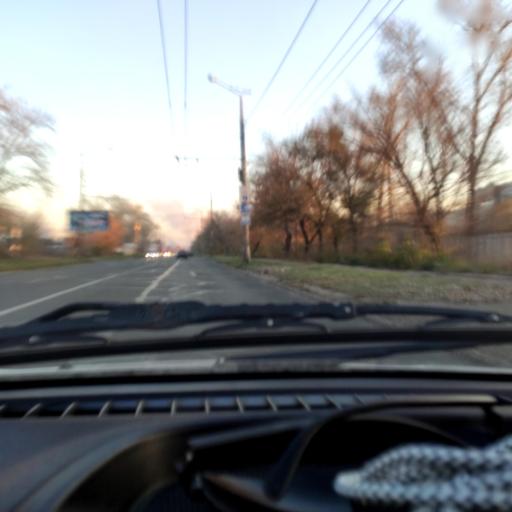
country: RU
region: Samara
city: Tol'yatti
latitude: 53.5280
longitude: 49.4366
